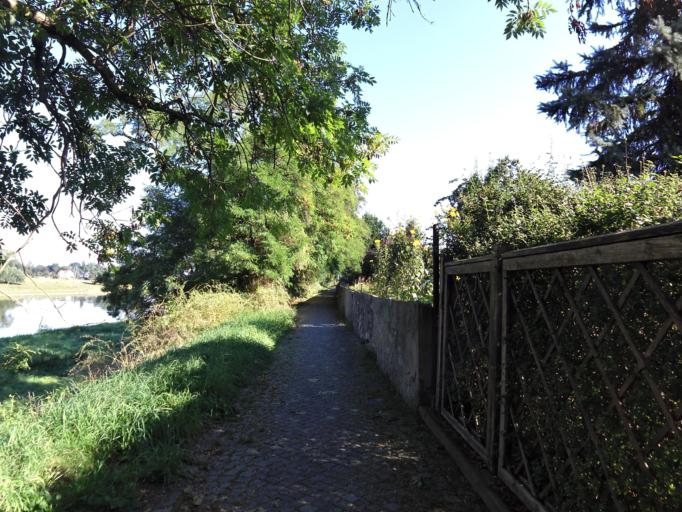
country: DE
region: Saxony
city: Nunchritz
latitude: 51.2660
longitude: 13.4050
